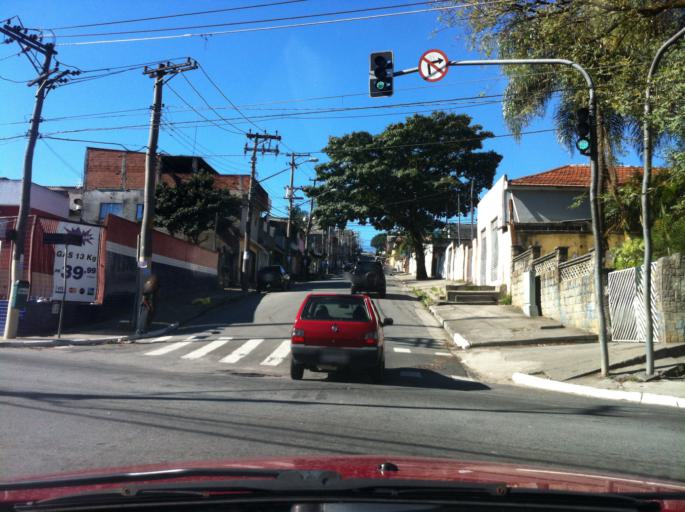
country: BR
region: Sao Paulo
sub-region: Ferraz De Vasconcelos
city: Ferraz de Vasconcelos
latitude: -23.5452
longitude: -46.4458
